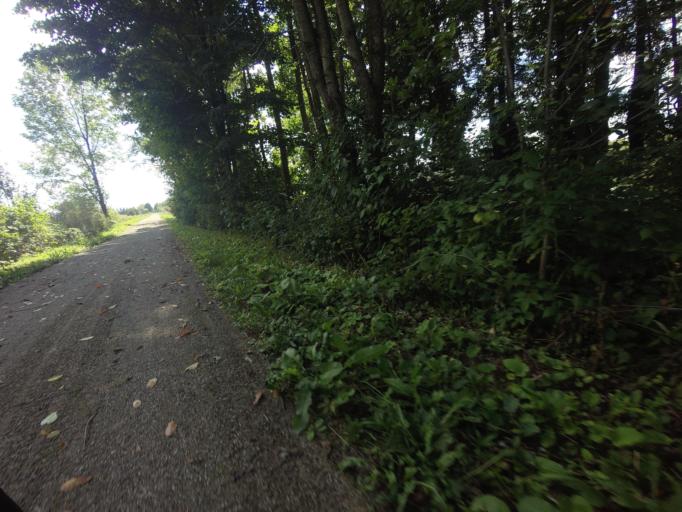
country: CA
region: Ontario
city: Huron East
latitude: 43.6864
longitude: -81.3143
